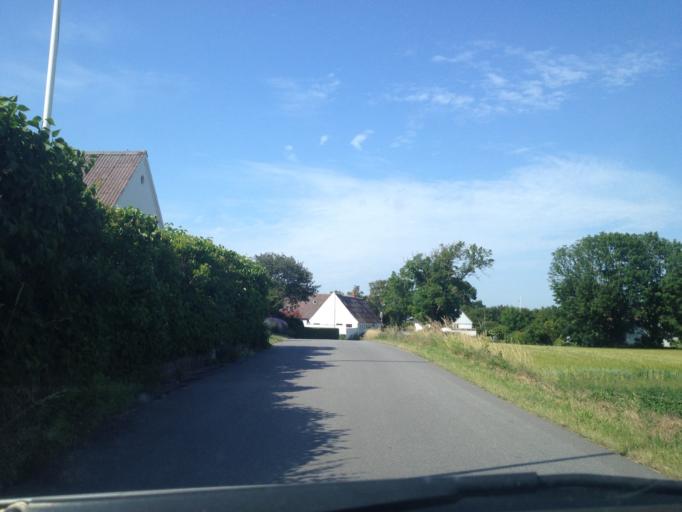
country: DK
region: Central Jutland
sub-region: Samso Kommune
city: Tranebjerg
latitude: 55.8373
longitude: 10.5551
